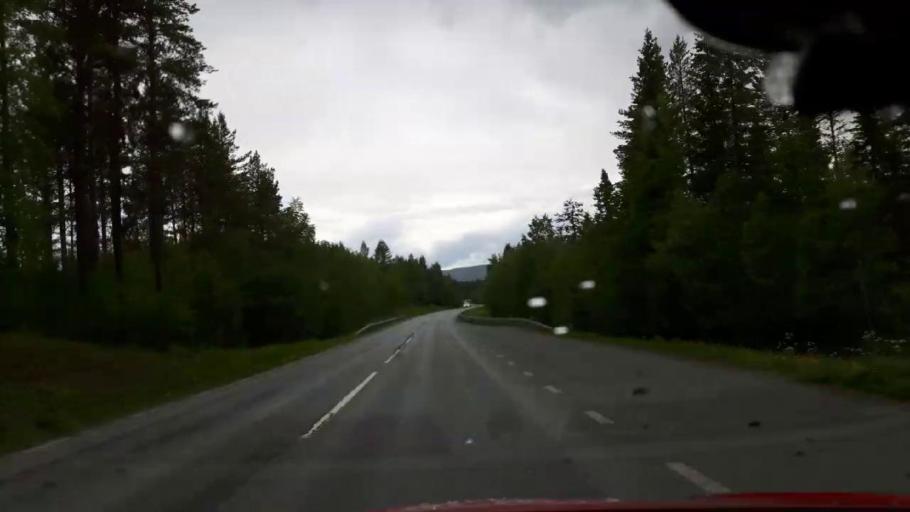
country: SE
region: Jaemtland
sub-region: Krokoms Kommun
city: Krokom
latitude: 63.4234
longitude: 14.2190
